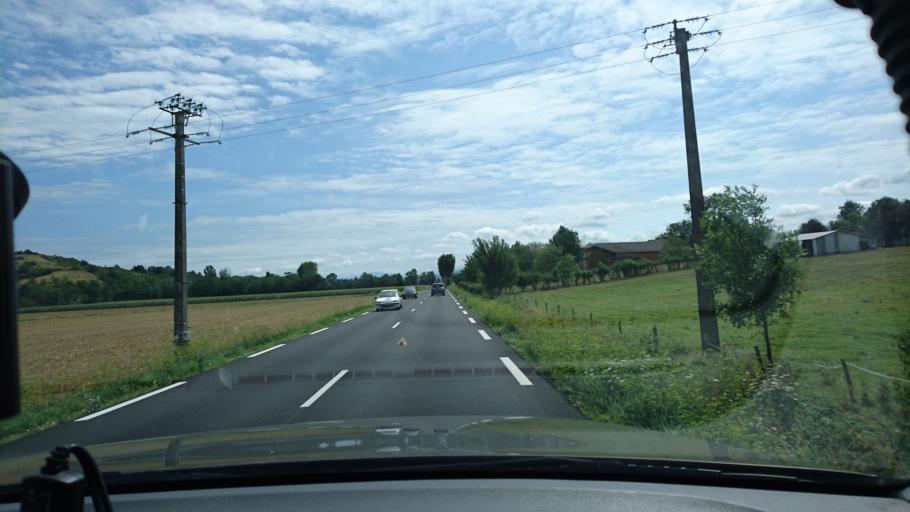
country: FR
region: Midi-Pyrenees
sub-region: Departement de l'Ariege
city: Lezat-sur-Leze
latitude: 43.2054
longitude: 1.3856
